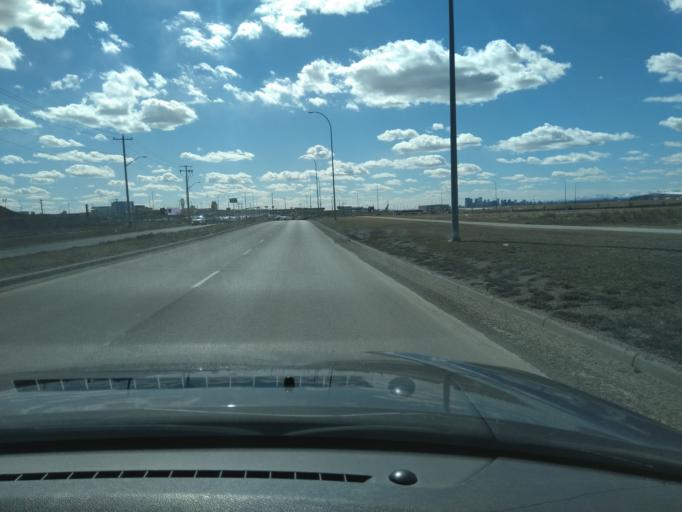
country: CA
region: Alberta
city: Calgary
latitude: 51.1419
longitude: -114.0135
